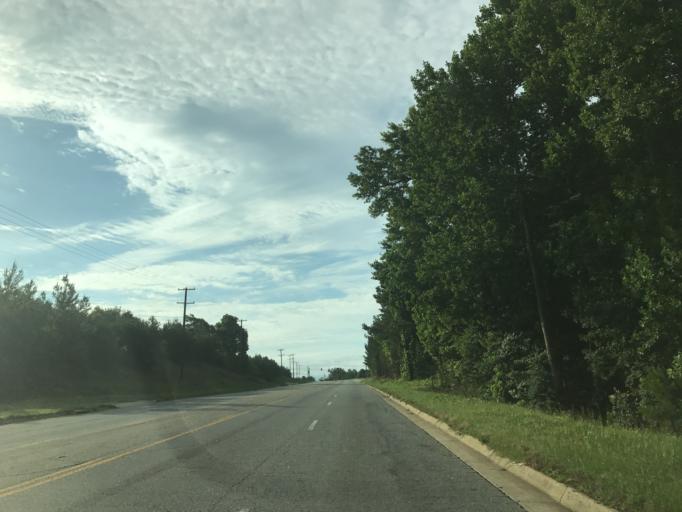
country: US
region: South Carolina
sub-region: Greenville County
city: Greer
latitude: 34.9055
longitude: -82.1955
